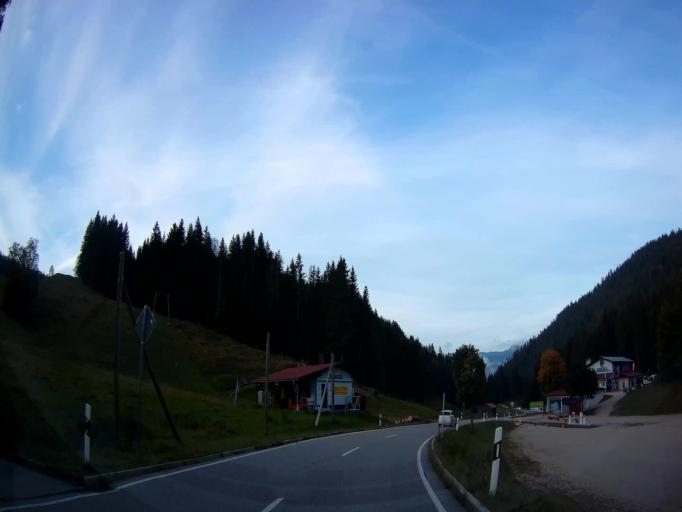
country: DE
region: Bavaria
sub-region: Upper Bavaria
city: Ramsau
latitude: 47.6266
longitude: 12.9044
